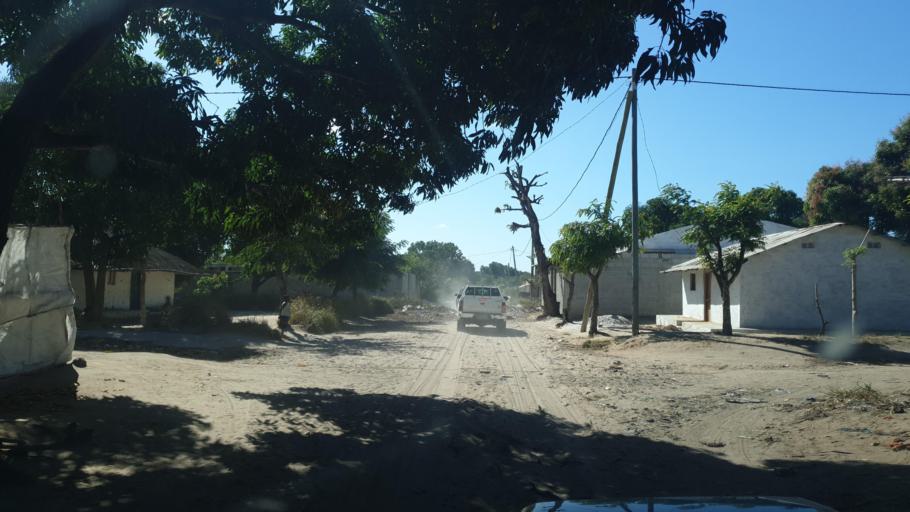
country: MZ
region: Nampula
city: Nacala
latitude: -14.5354
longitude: 40.7034
